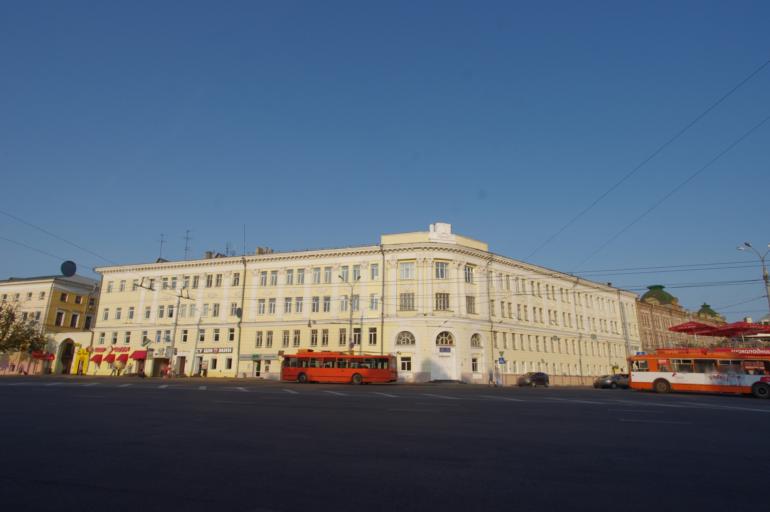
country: RU
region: Nizjnij Novgorod
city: Nizhniy Novgorod
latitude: 56.3276
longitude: 44.0066
